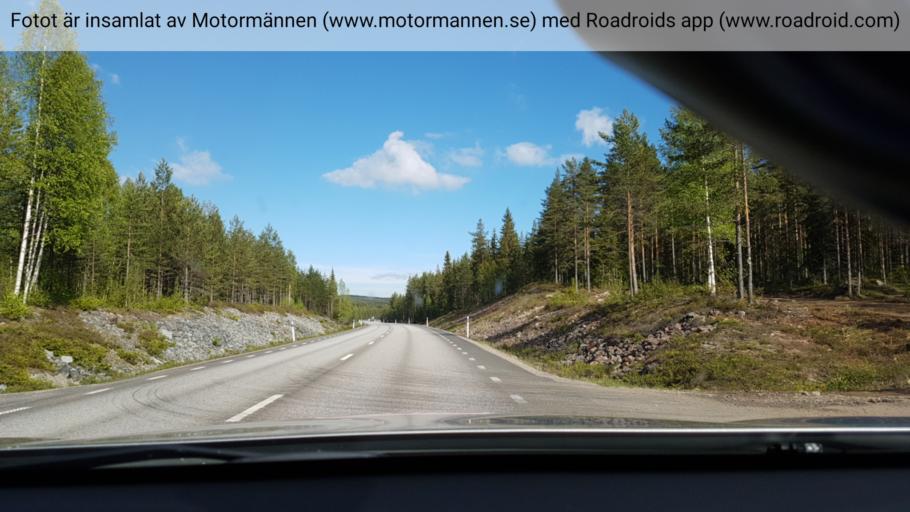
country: SE
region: Dalarna
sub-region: Faluns Kommun
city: Bjursas
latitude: 60.7855
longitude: 15.2941
